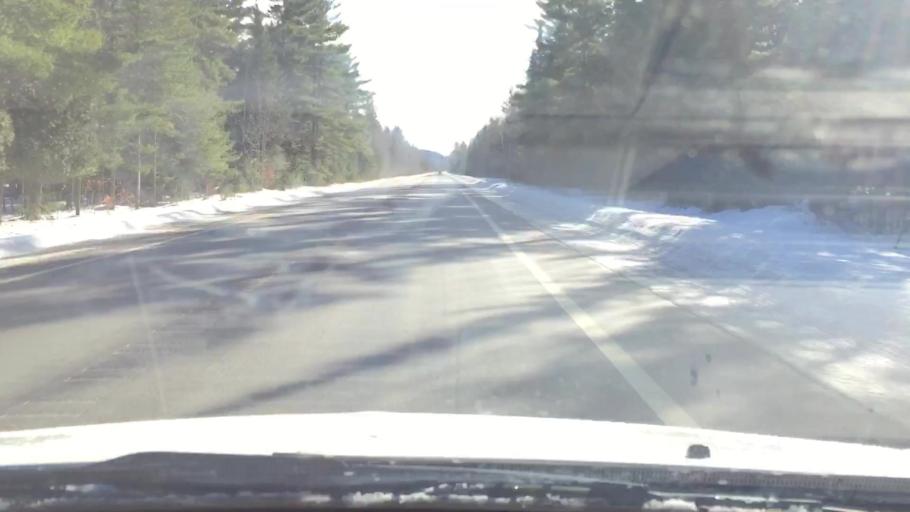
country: US
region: Michigan
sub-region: Antrim County
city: Mancelona
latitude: 45.0312
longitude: -85.0668
